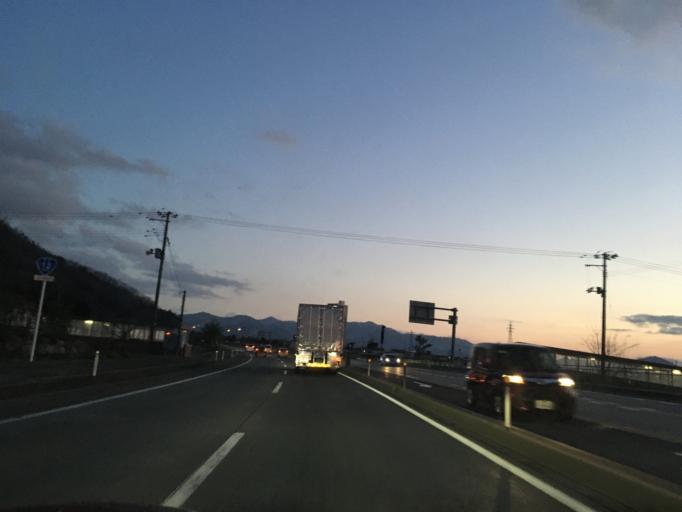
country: JP
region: Yamagata
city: Kaminoyama
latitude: 38.1498
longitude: 140.2905
